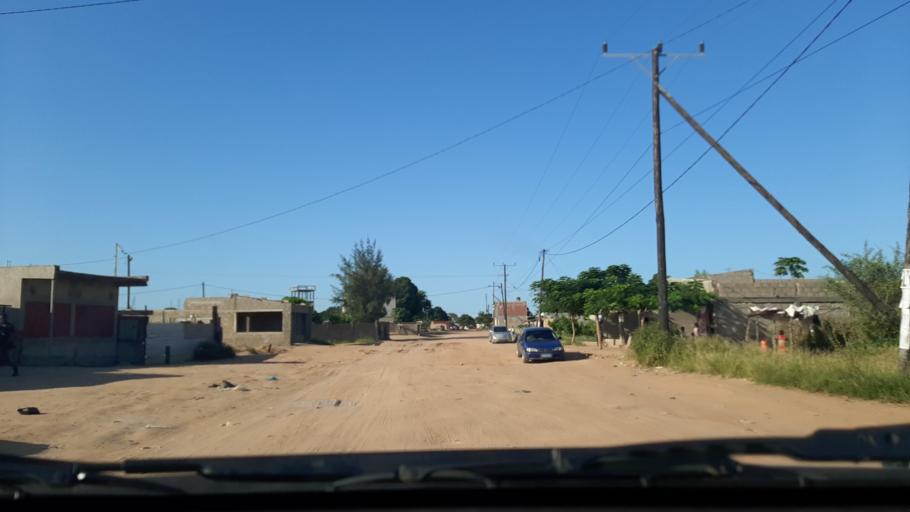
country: MZ
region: Maputo City
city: Maputo
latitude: -25.8026
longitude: 32.5477
